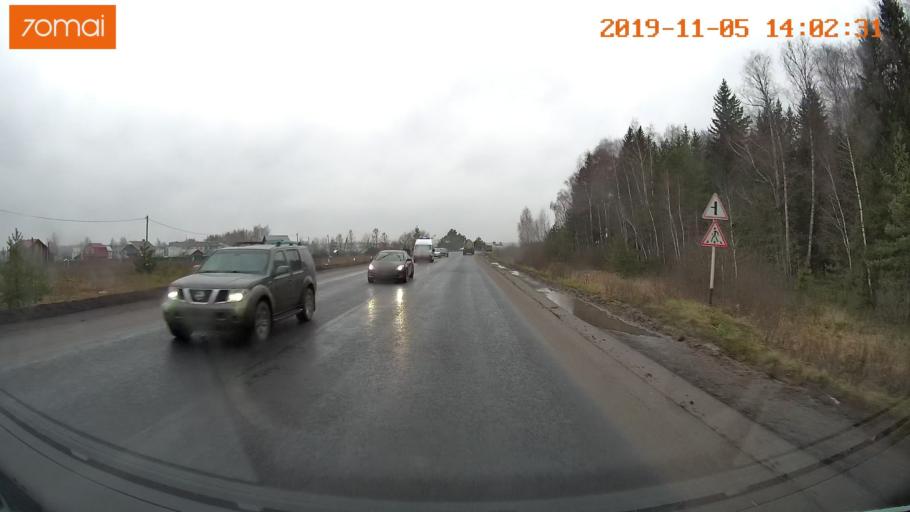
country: RU
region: Ivanovo
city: Kokhma
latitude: 57.0012
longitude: 41.2121
